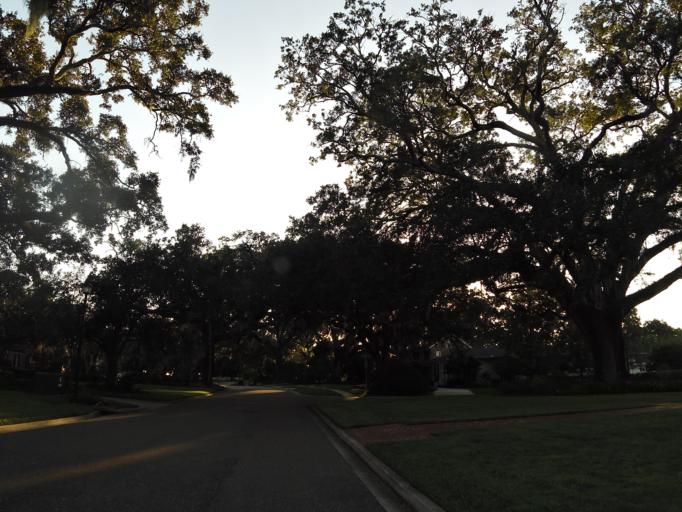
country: US
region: Florida
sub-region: Duval County
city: Jacksonville
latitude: 30.3017
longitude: -81.6533
